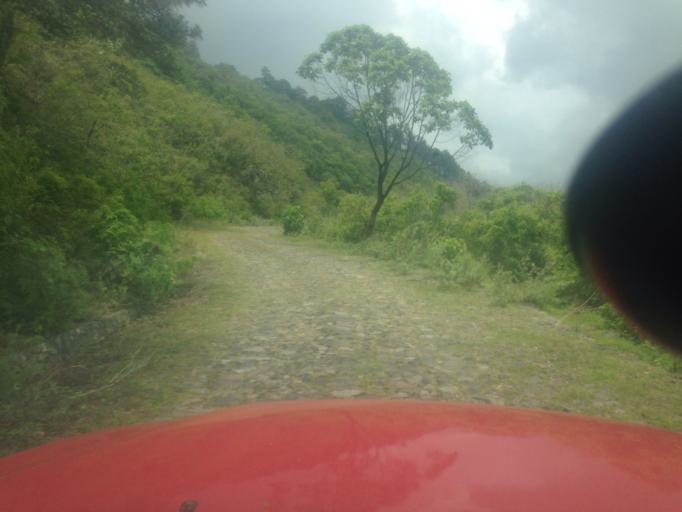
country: MX
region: Nayarit
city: Jala
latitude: 21.1283
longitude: -104.5004
